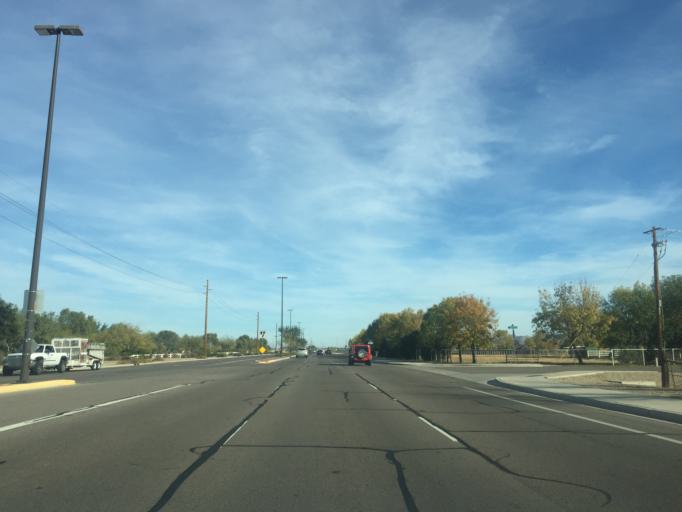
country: US
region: Arizona
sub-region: Maricopa County
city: Queen Creek
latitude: 33.2192
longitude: -111.7516
